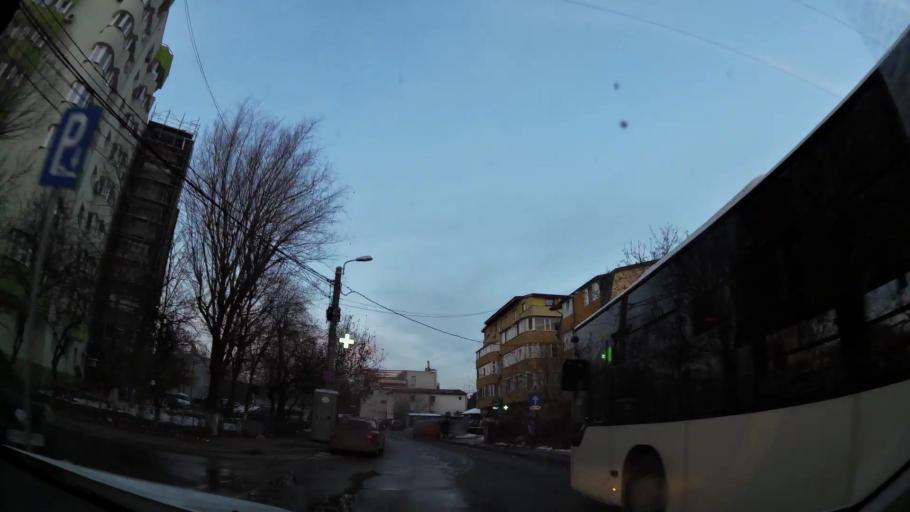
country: RO
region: Ilfov
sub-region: Comuna Fundeni-Dobroesti
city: Fundeni
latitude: 44.4644
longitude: 26.1482
